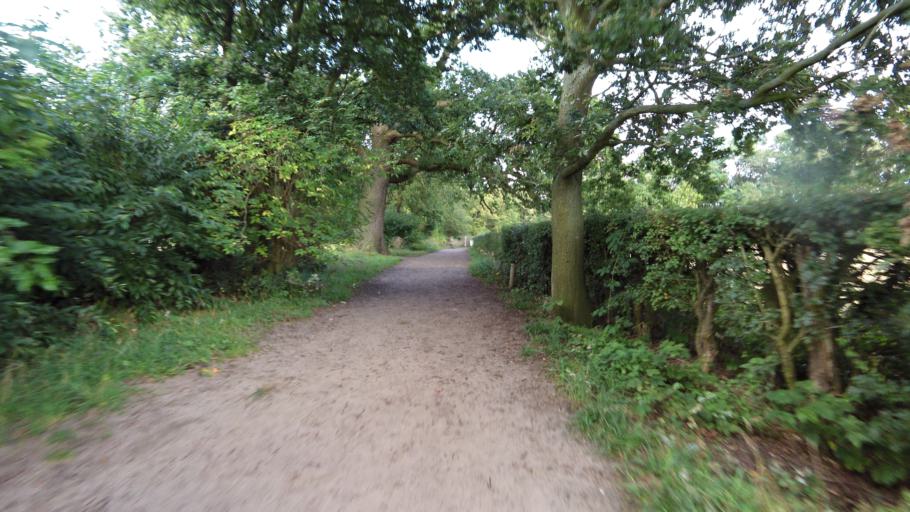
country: NL
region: Utrecht
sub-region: Gemeente De Bilt
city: De Bilt
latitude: 52.1124
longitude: 5.2015
